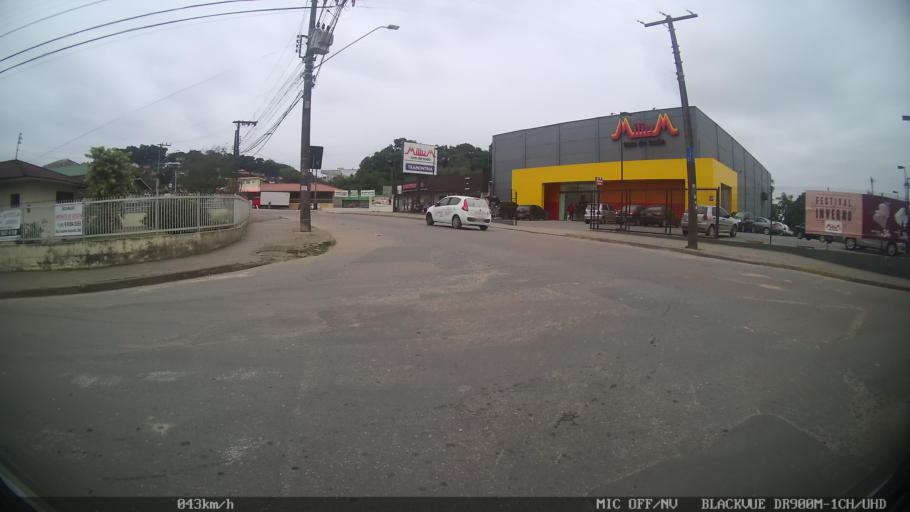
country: BR
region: Santa Catarina
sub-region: Joinville
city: Joinville
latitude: -26.3607
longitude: -48.8286
